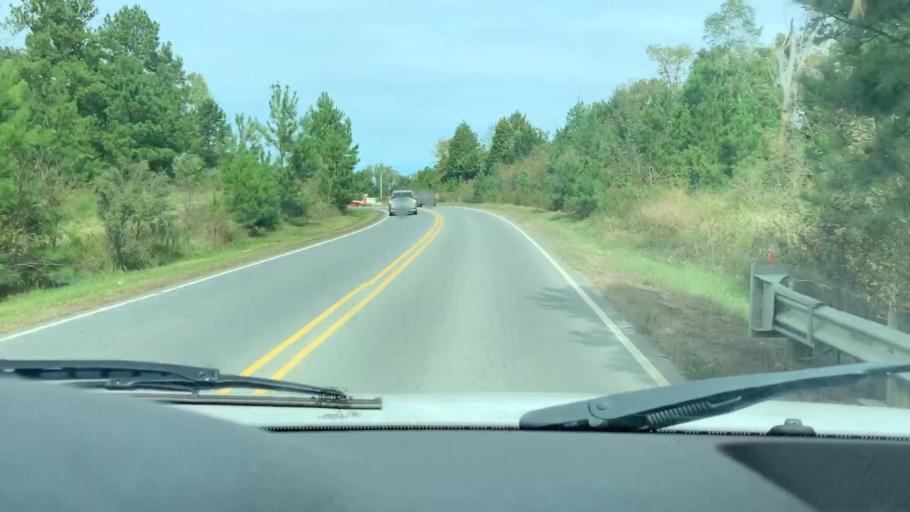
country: US
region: North Carolina
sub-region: Mecklenburg County
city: Huntersville
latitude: 35.4393
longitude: -80.7642
